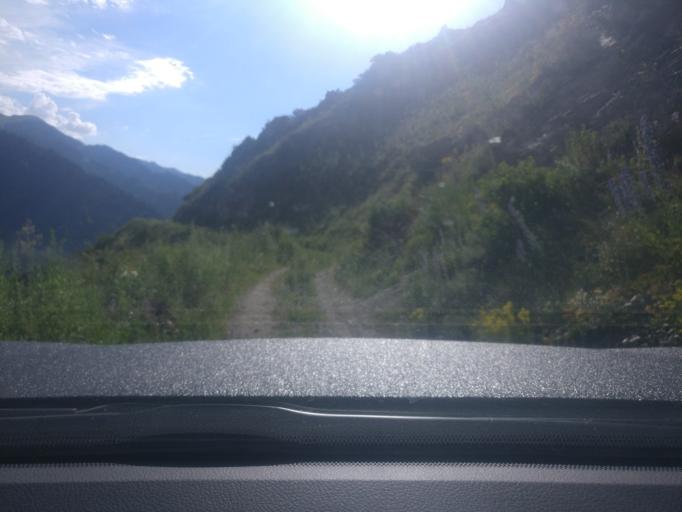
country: KZ
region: Almaty Qalasy
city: Almaty
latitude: 43.1069
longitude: 76.9435
